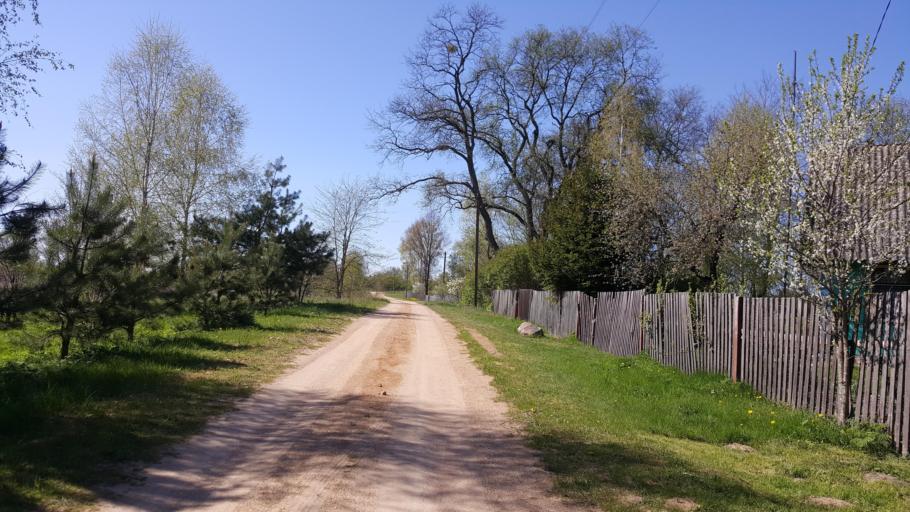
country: BY
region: Brest
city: Kamyanyets
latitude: 52.4504
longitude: 23.8926
